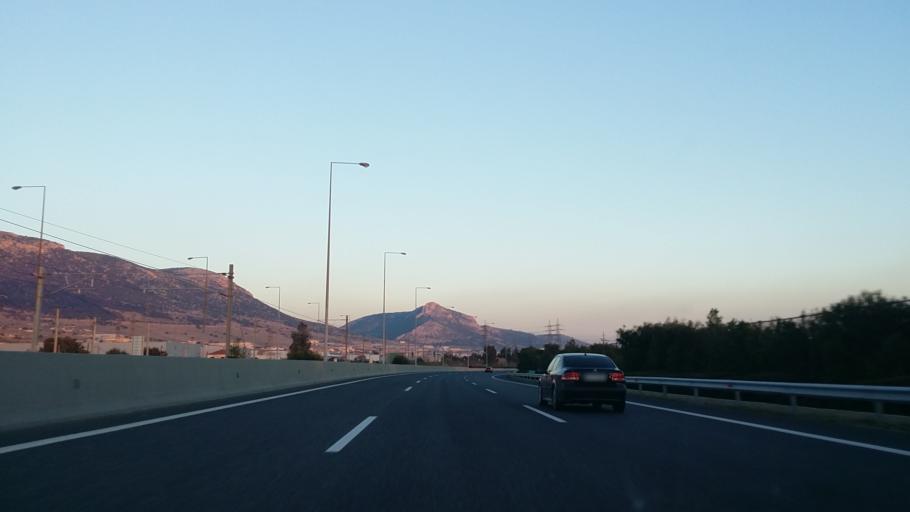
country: GR
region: Attica
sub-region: Nomarchia Dytikis Attikis
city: Aspropyrgos
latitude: 38.0943
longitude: 23.5698
